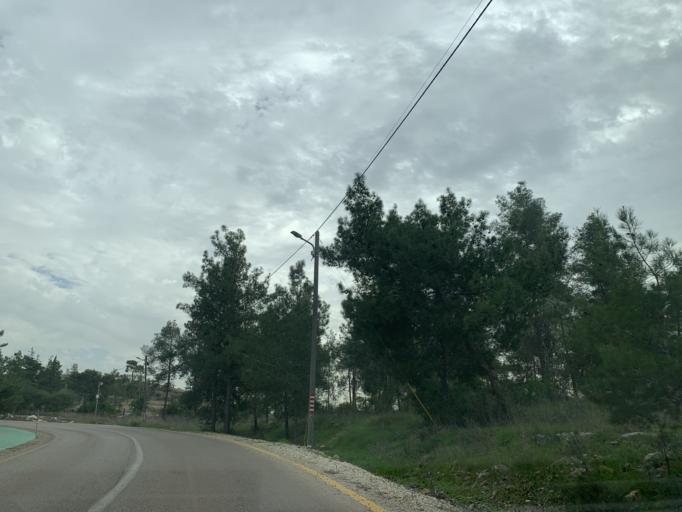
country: IL
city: Nirit
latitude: 32.1438
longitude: 34.9837
